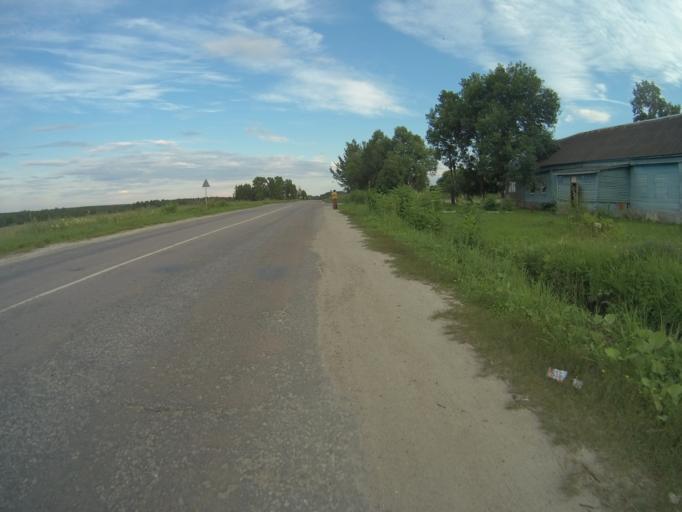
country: RU
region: Vladimir
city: Sudogda
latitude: 55.9802
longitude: 40.8476
